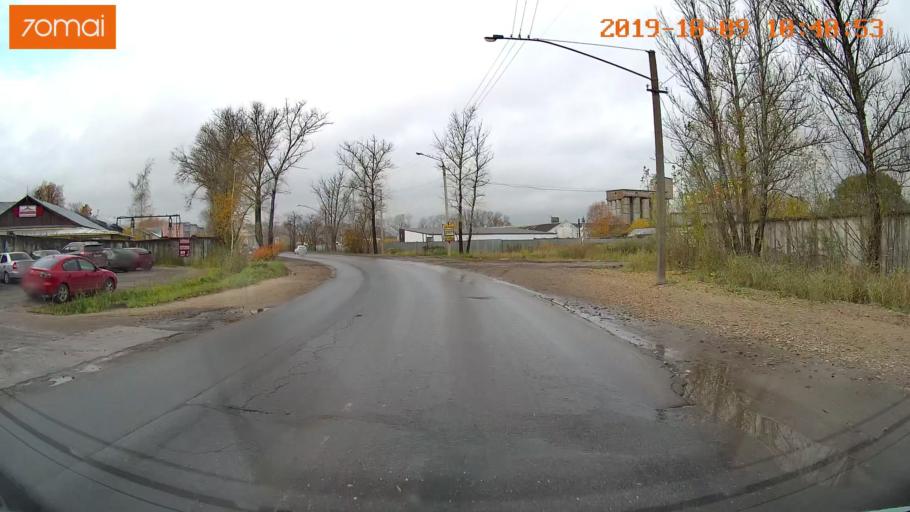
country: RU
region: Vologda
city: Vologda
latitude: 59.2343
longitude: 39.8338
